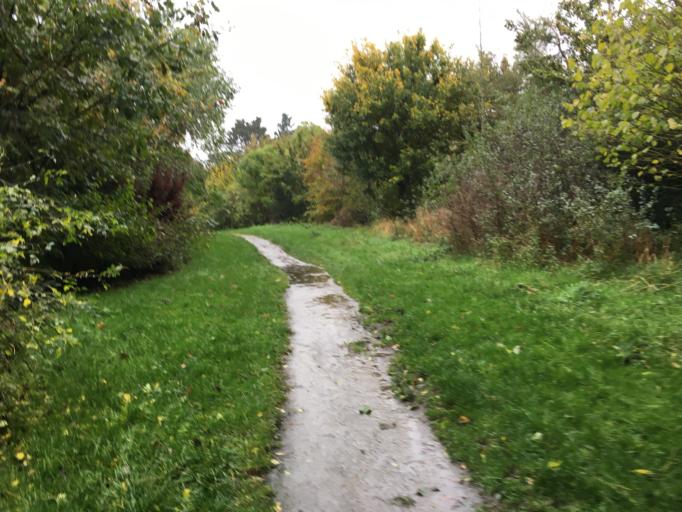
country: GB
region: England
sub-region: Warwickshire
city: Rugby
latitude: 52.3703
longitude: -1.2372
